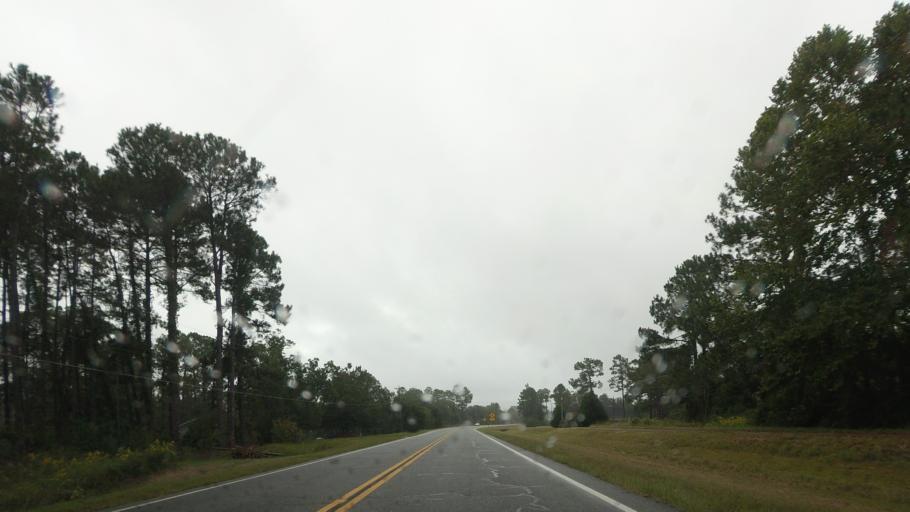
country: US
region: Georgia
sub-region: Ben Hill County
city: Fitzgerald
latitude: 31.7661
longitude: -83.2452
